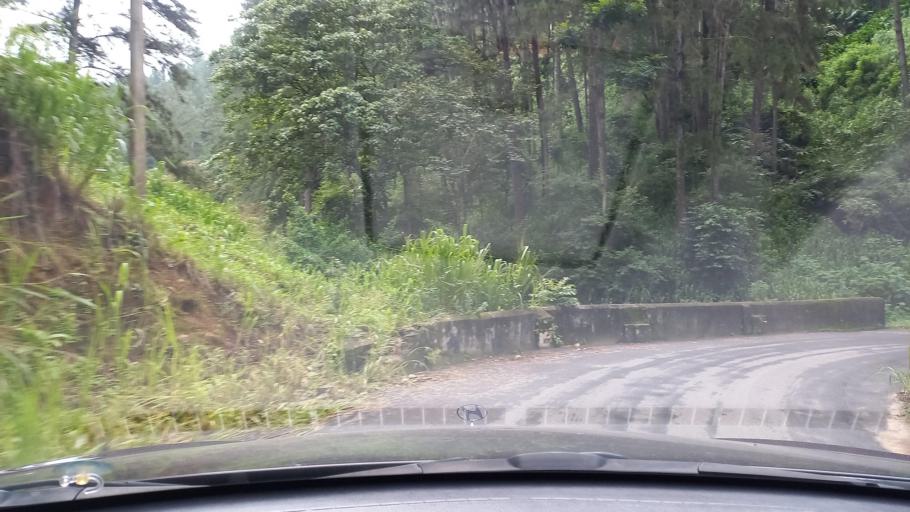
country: LK
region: Central
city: Gampola
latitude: 7.2138
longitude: 80.6203
